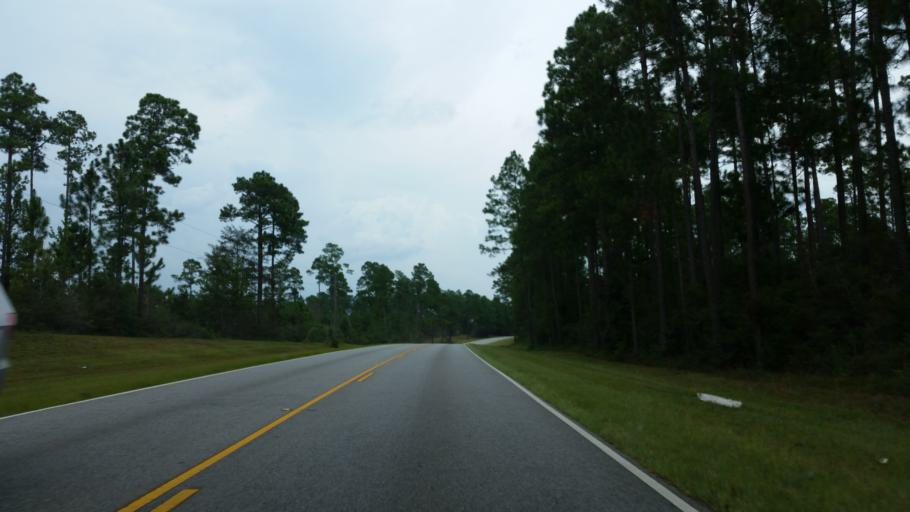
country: US
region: Florida
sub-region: Escambia County
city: Cantonment
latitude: 30.6605
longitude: -87.3024
